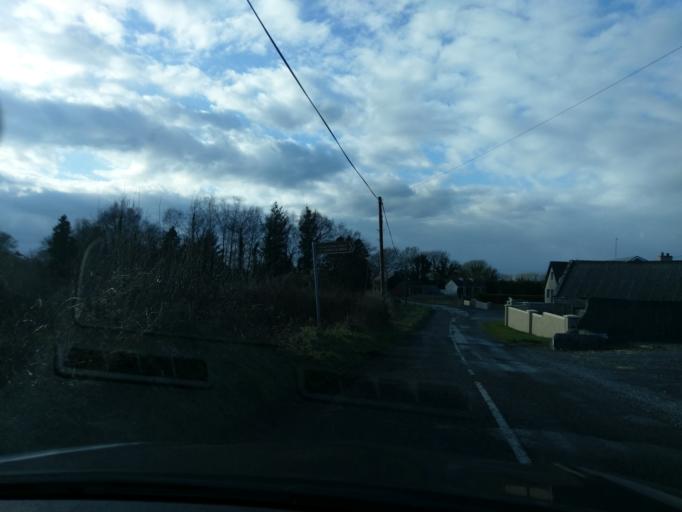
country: IE
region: Connaught
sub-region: County Galway
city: Athenry
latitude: 53.3826
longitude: -8.5826
